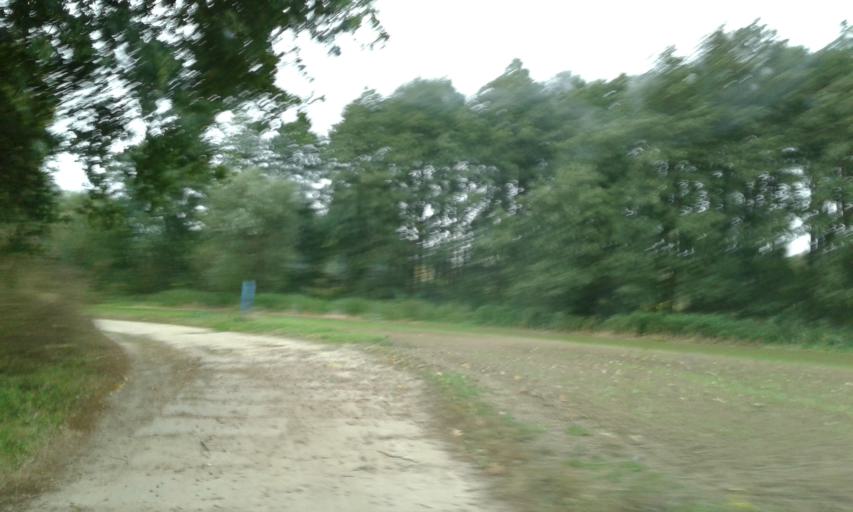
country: PL
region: West Pomeranian Voivodeship
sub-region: Powiat stargardzki
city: Dolice
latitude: 53.1046
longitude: 15.2269
